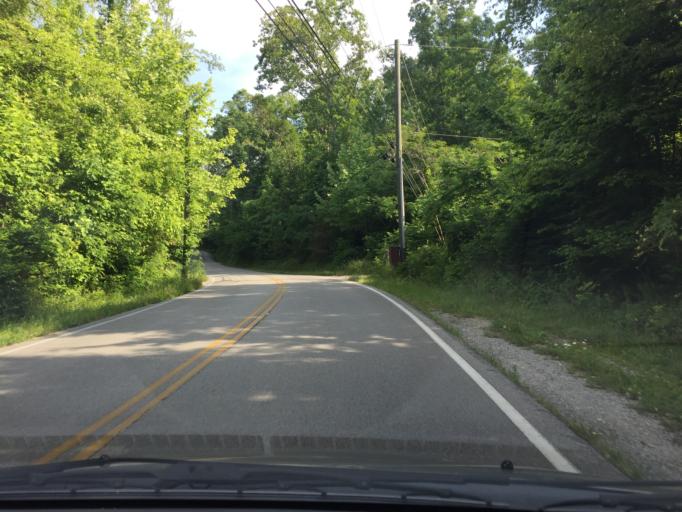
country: US
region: Tennessee
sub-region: Hamilton County
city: Collegedale
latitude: 35.0826
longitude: -85.0093
